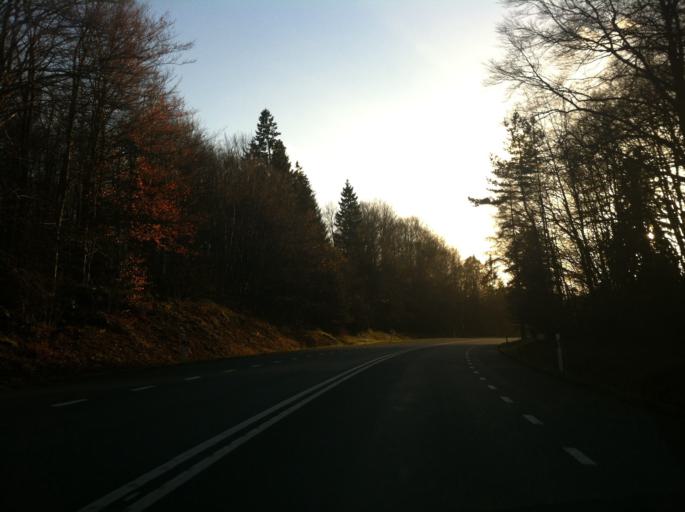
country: SE
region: Skane
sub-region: Hassleholms Kommun
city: Hassleholm
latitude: 56.1460
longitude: 13.8044
